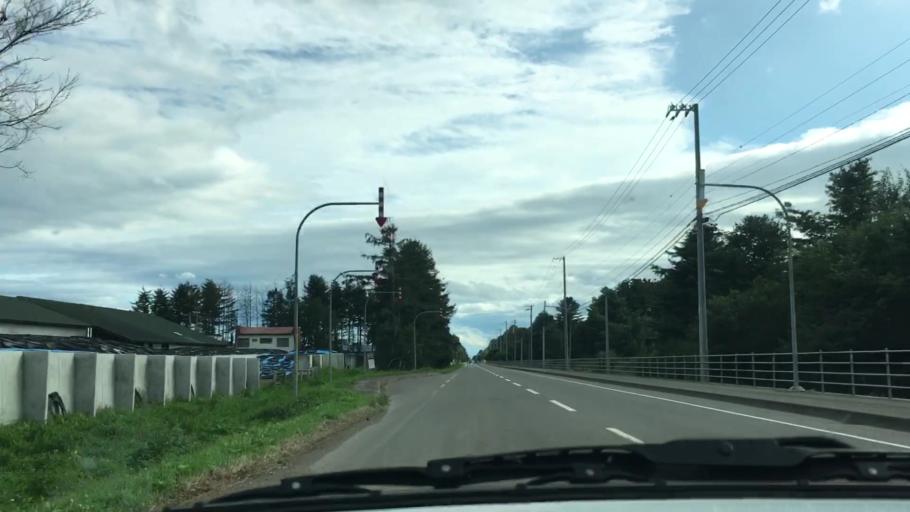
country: JP
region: Hokkaido
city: Otofuke
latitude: 43.2496
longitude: 143.2989
